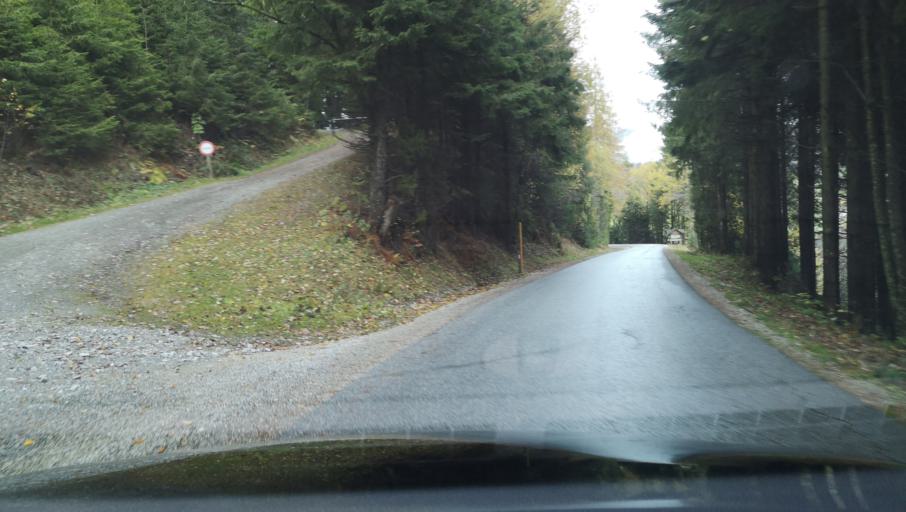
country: AT
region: Styria
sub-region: Politischer Bezirk Weiz
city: Gasen
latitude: 47.3617
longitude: 15.5819
